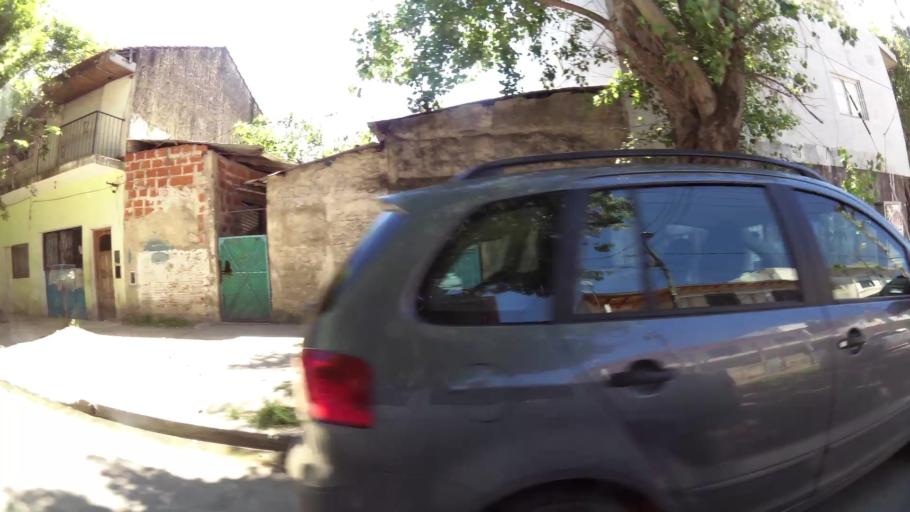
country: AR
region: Buenos Aires
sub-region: Partido de Tigre
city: Tigre
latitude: -34.5041
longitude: -58.5847
